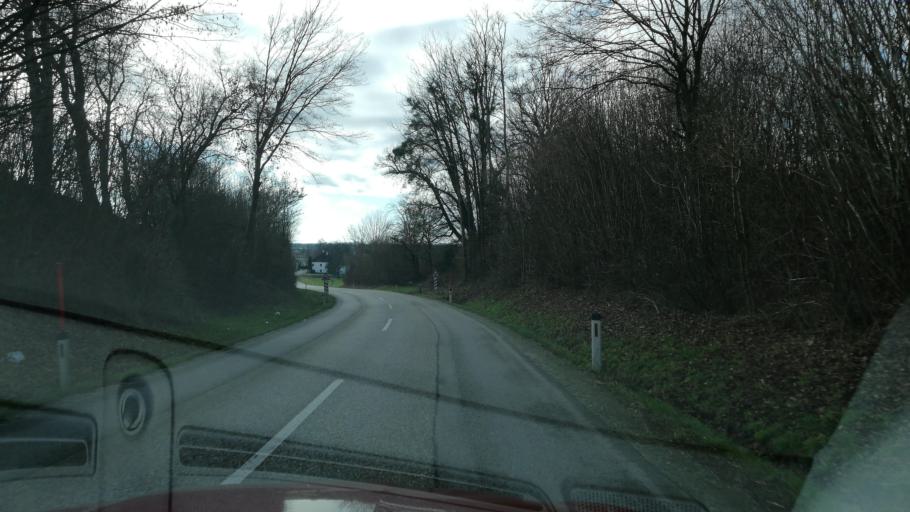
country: AT
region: Upper Austria
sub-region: Politischer Bezirk Braunau am Inn
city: Braunau am Inn
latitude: 48.2146
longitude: 13.1075
